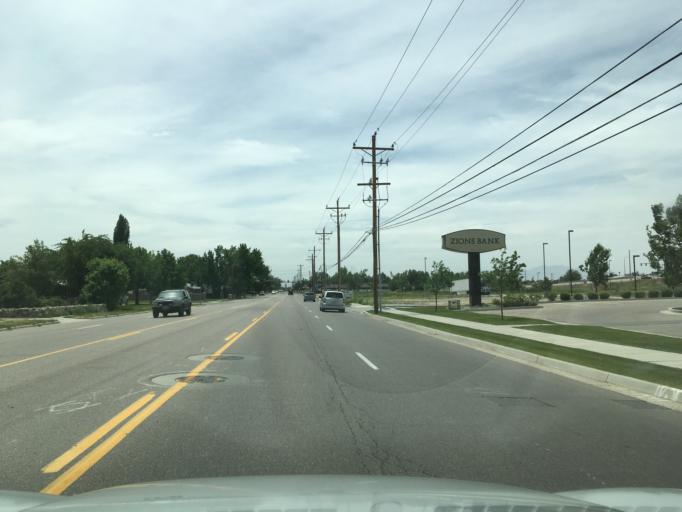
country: US
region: Utah
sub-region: Davis County
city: Layton
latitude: 41.0587
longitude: -111.9577
